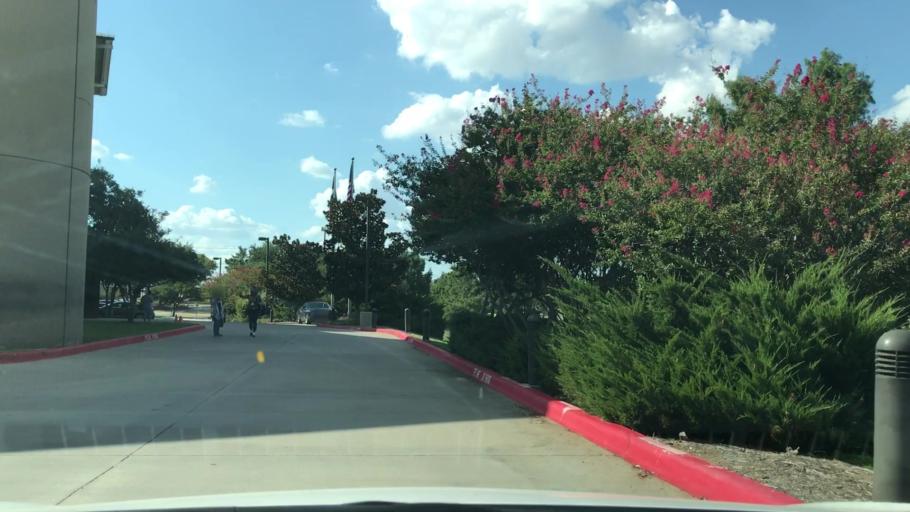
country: US
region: Texas
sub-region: Dallas County
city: Coppell
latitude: 32.9143
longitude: -96.9841
